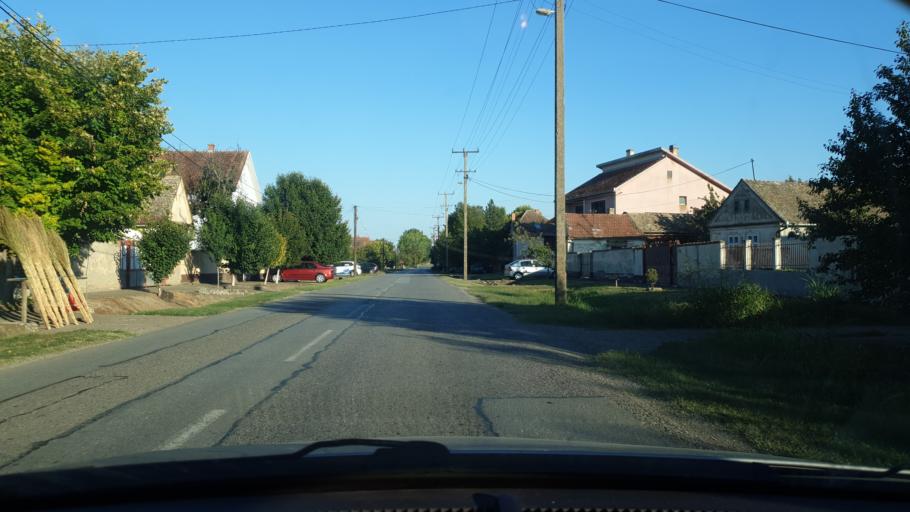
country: RS
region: Autonomna Pokrajina Vojvodina
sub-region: Sremski Okrug
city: Ruma
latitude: 44.9753
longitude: 19.8885
